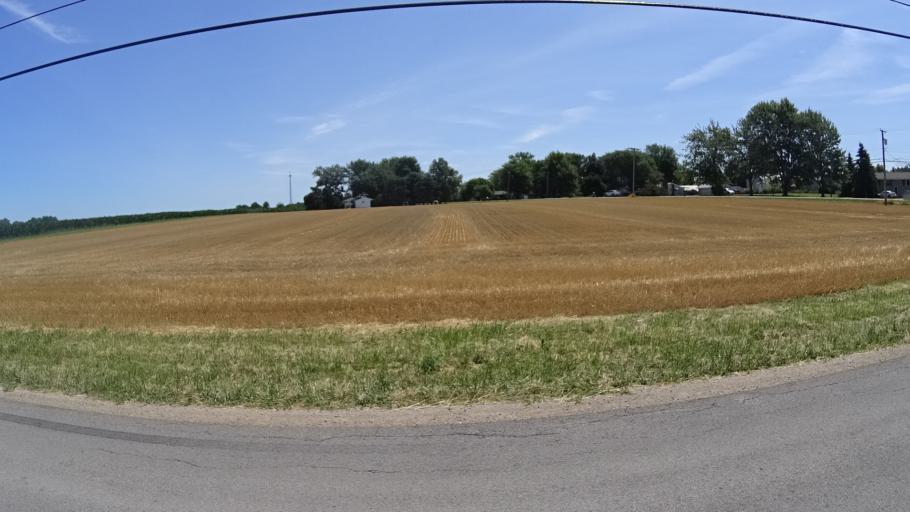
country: US
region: Ohio
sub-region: Ottawa County
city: Port Clinton
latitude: 41.4317
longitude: -82.8478
